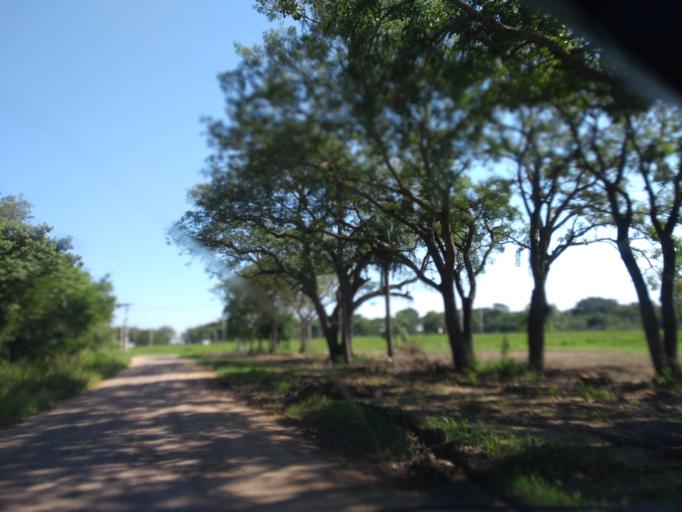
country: AR
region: Chaco
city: Barranqueras
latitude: -27.4377
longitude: -58.9155
